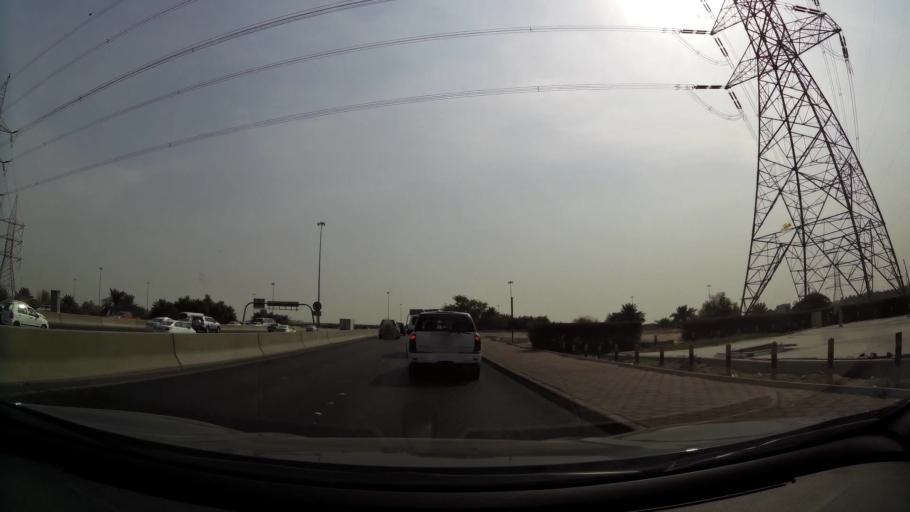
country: KW
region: Al Asimah
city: Ar Rabiyah
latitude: 29.3034
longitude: 47.9447
